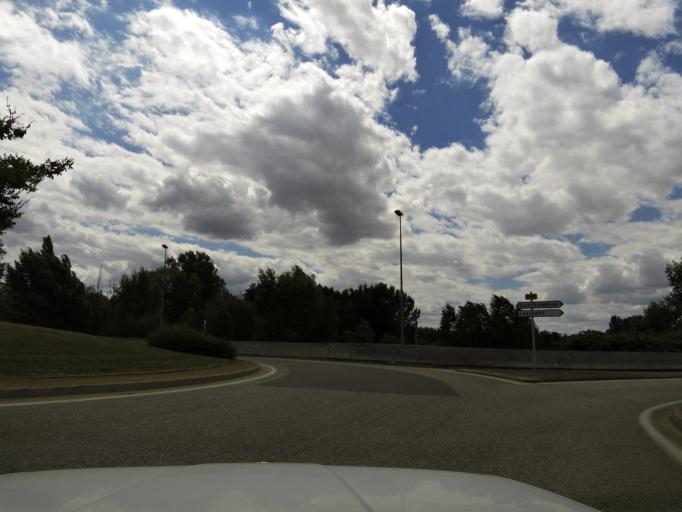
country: FR
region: Rhone-Alpes
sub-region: Departement de l'Isere
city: Saint-Romain-de-Jalionas
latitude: 45.7608
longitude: 5.2086
